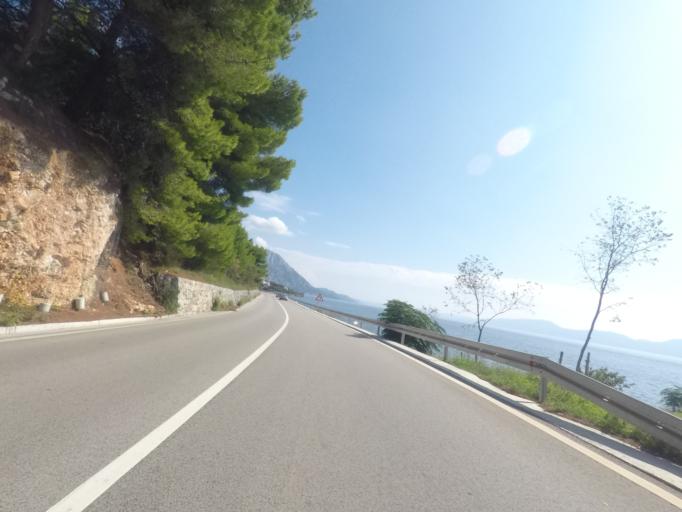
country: HR
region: Splitsko-Dalmatinska
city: Vrgorac
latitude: 43.1280
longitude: 17.2900
